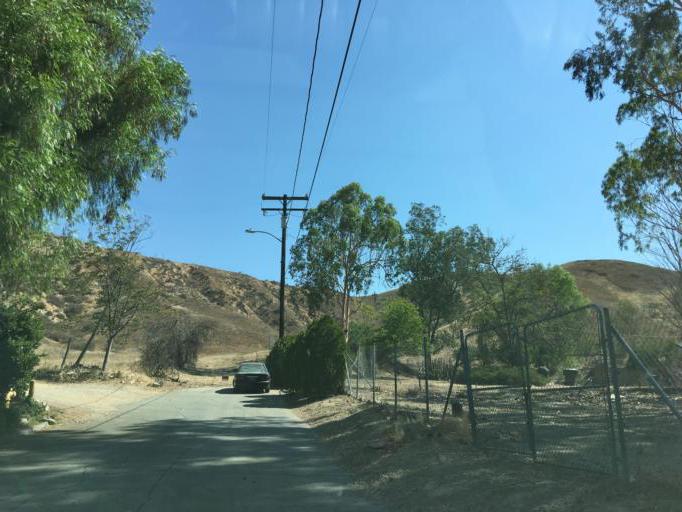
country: US
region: California
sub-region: Los Angeles County
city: Val Verde
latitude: 34.4477
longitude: -118.6496
